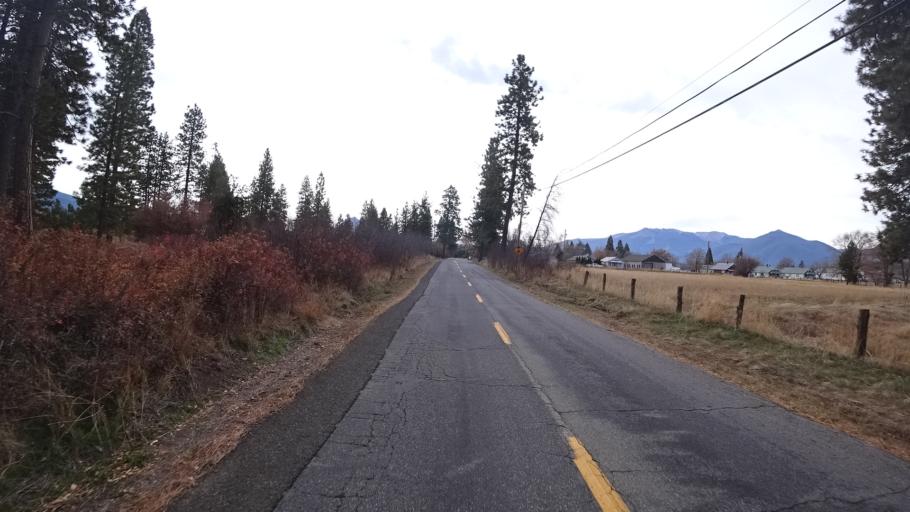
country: US
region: California
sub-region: Siskiyou County
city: Weed
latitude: 41.4403
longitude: -122.3765
